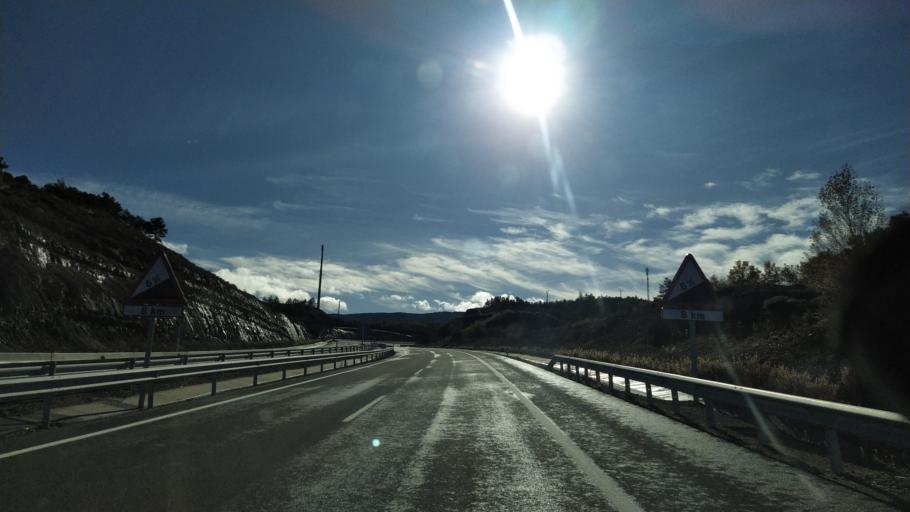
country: ES
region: Aragon
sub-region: Provincia de Huesca
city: Arguis
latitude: 42.3990
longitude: -0.3730
